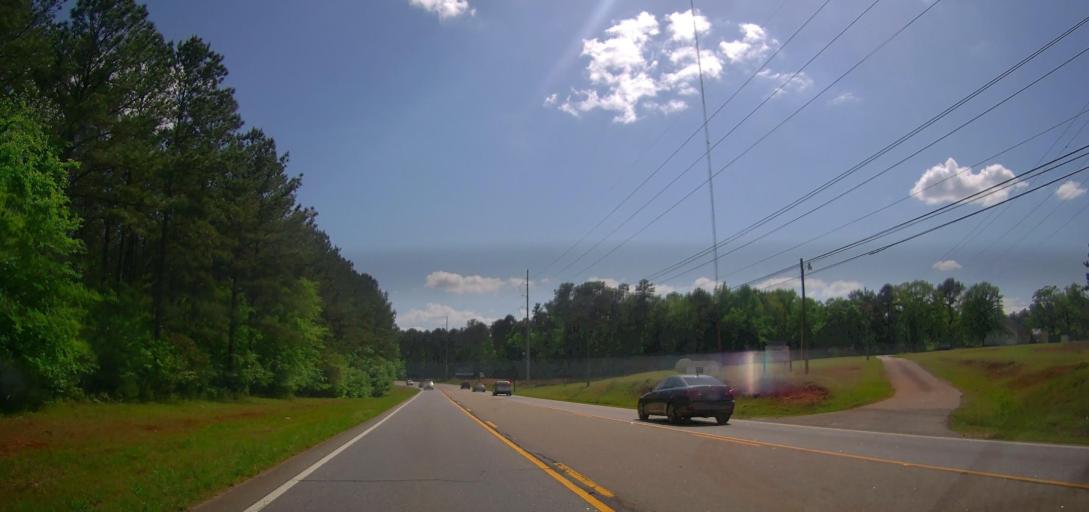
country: US
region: Georgia
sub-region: Putnam County
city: Jefferson
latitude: 33.4756
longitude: -83.2445
